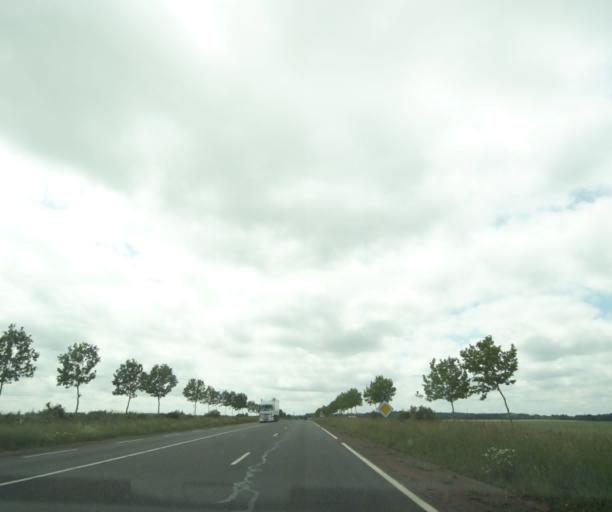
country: FR
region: Poitou-Charentes
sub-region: Departement des Deux-Sevres
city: Saint-Varent
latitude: 46.8443
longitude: -0.2087
